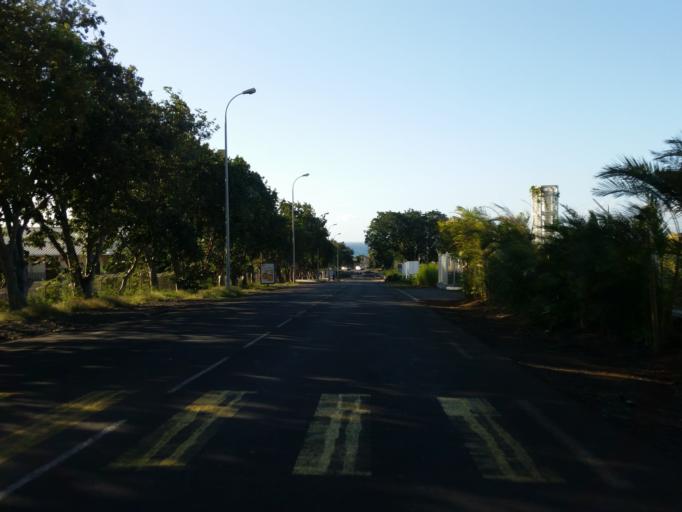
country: RE
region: Reunion
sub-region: Reunion
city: Saint-Denis
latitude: -20.8899
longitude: 55.4719
